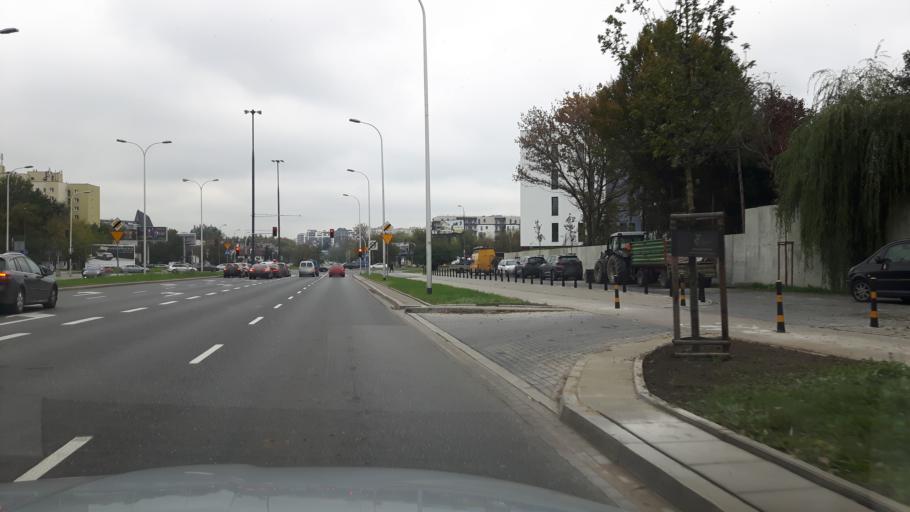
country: PL
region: Masovian Voivodeship
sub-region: Warszawa
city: Mokotow
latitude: 52.1748
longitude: 21.0463
